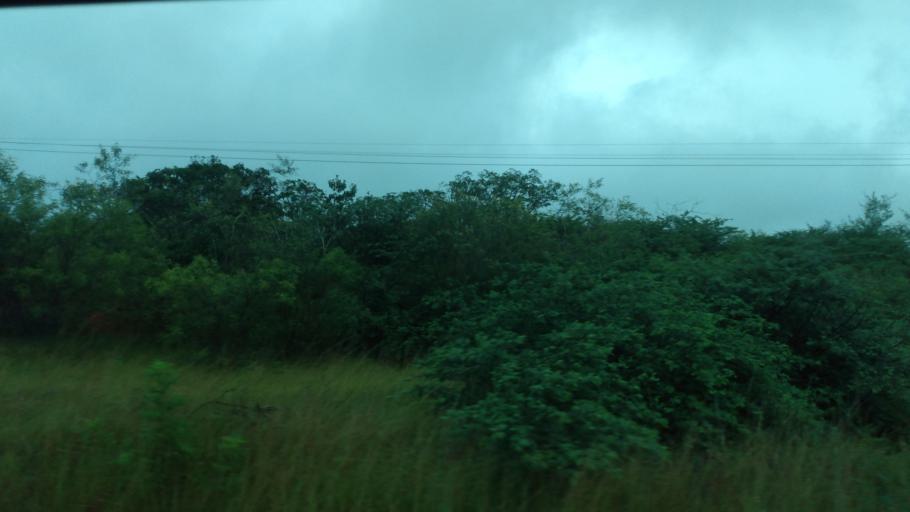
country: BR
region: Pernambuco
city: Garanhuns
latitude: -8.8563
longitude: -36.5125
